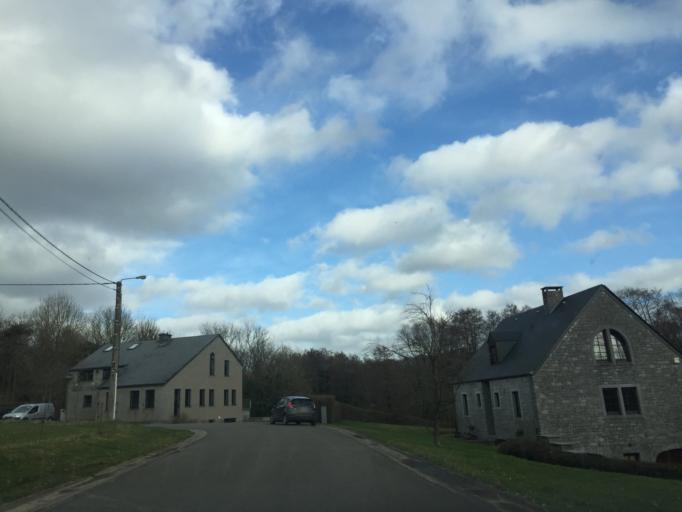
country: BE
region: Wallonia
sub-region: Province du Luxembourg
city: Durbuy
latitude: 50.3082
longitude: 5.4836
